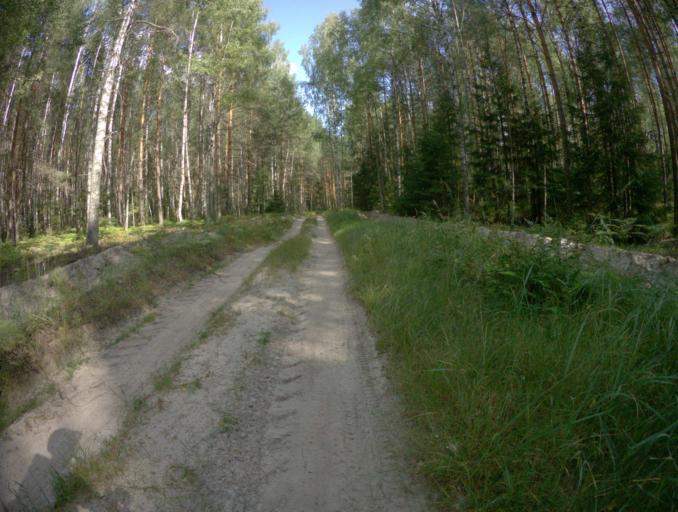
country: RU
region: Vladimir
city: Vorsha
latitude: 55.9087
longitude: 40.1670
